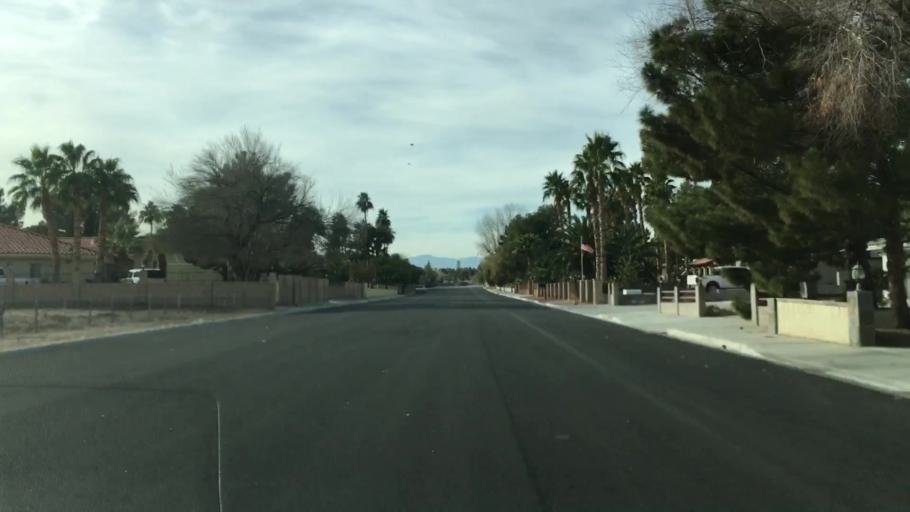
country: US
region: Nevada
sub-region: Clark County
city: Whitney
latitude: 36.0823
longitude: -115.0934
